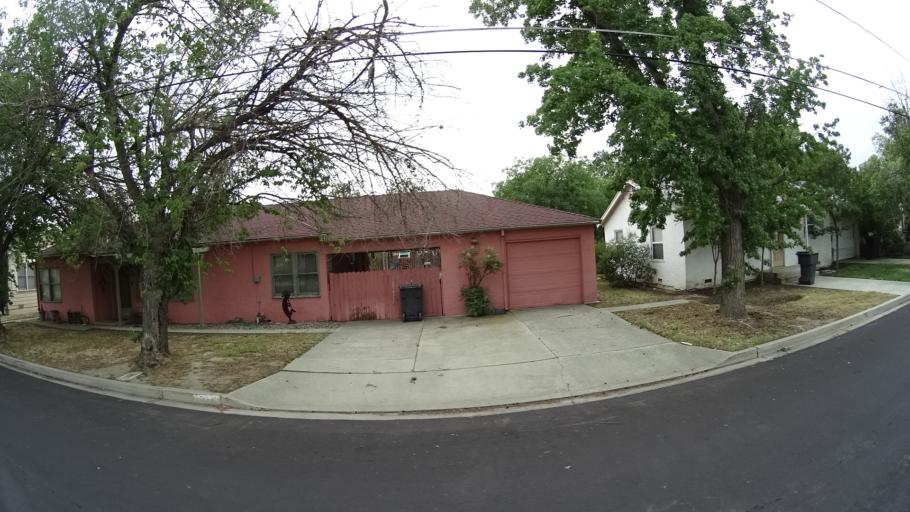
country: US
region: California
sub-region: Kings County
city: Hanford
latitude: 36.3381
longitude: -119.6506
